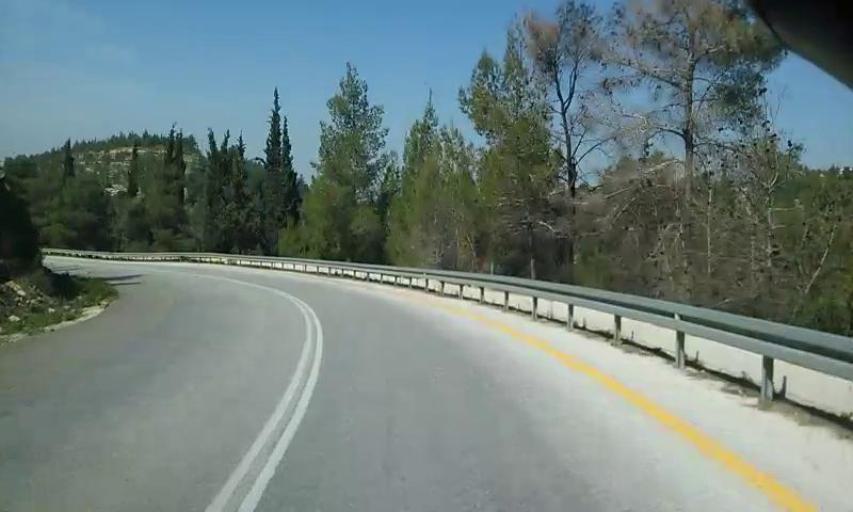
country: PS
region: West Bank
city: Nahhalin
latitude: 31.6737
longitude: 35.1034
